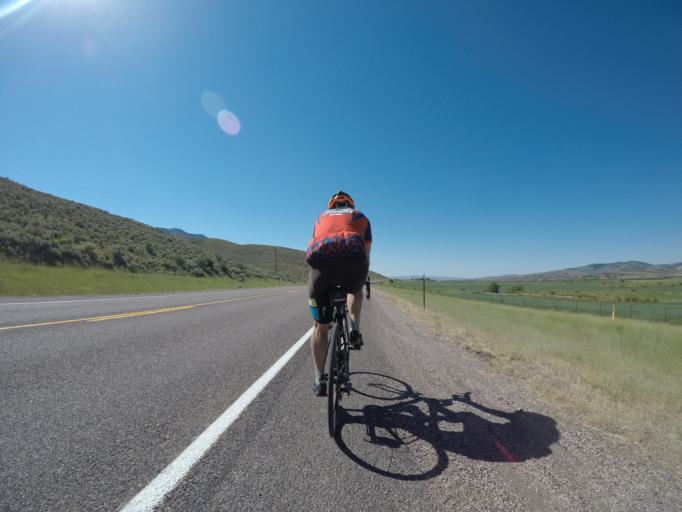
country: US
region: Idaho
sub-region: Bear Lake County
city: Montpelier
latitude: 42.3830
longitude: -111.0526
